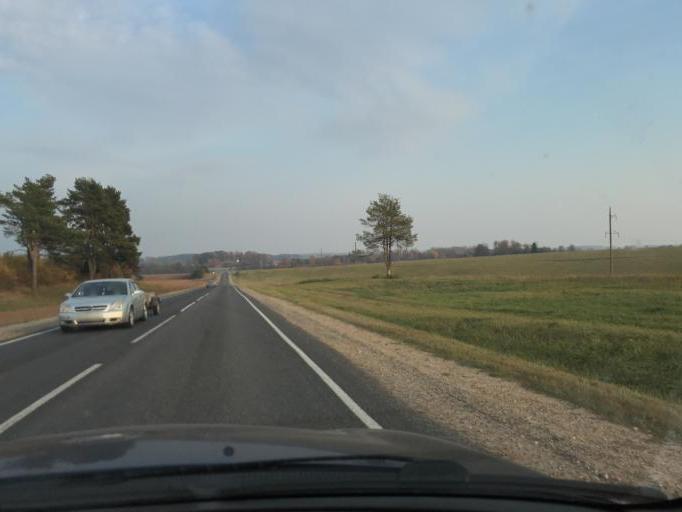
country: BY
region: Grodnenskaya
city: Navahrudak
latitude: 53.5908
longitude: 25.9474
